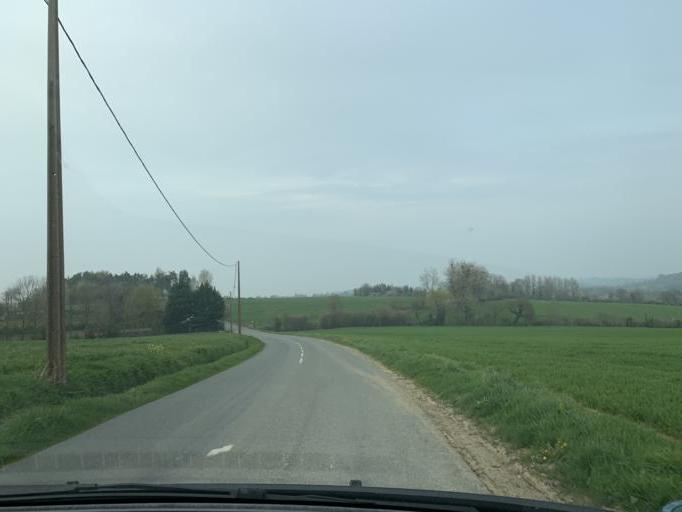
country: FR
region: Nord-Pas-de-Calais
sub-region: Departement du Pas-de-Calais
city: Longfosse
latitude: 50.6942
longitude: 1.7743
